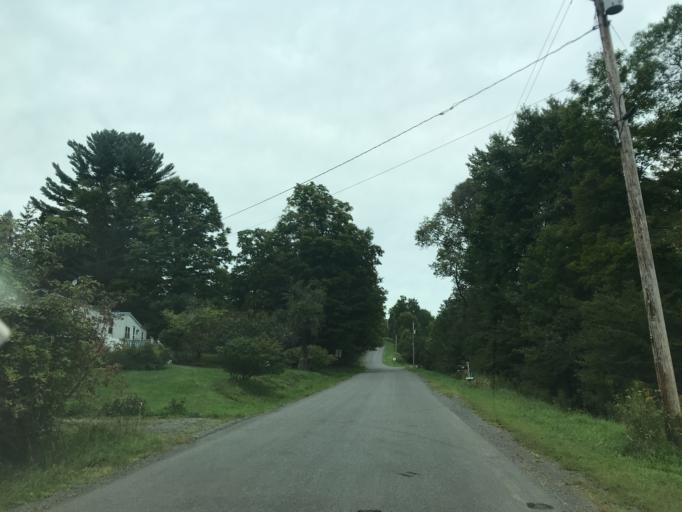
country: US
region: New York
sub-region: Otsego County
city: Worcester
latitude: 42.5204
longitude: -74.6655
